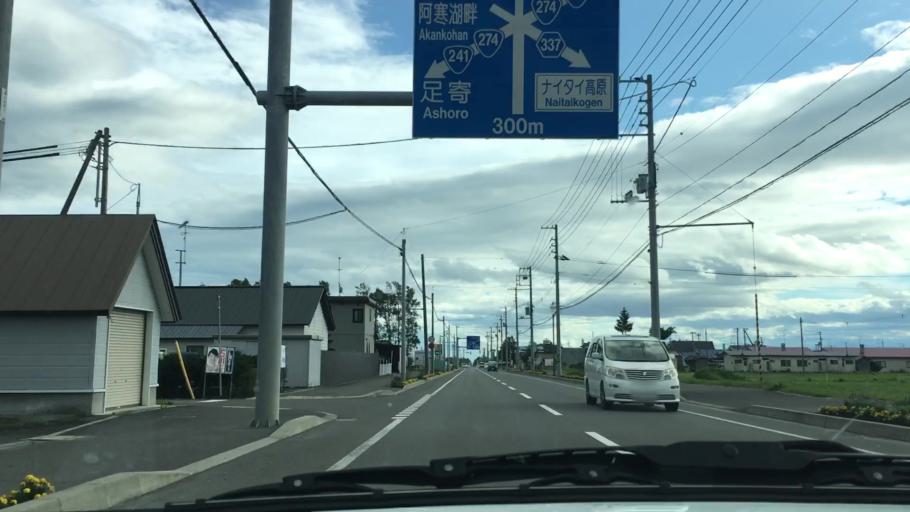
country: JP
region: Hokkaido
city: Otofuke
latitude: 43.2280
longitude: 143.2940
